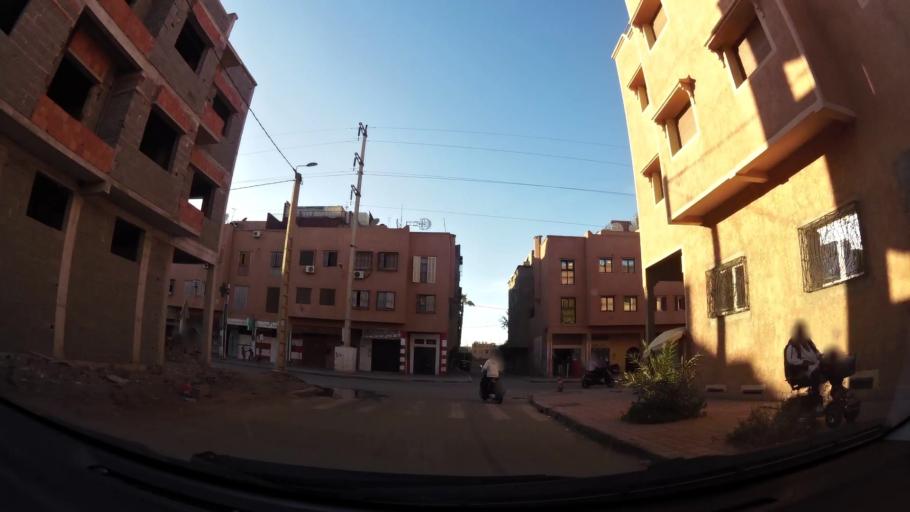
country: MA
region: Marrakech-Tensift-Al Haouz
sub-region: Marrakech
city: Marrakesh
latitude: 31.6175
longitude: -8.0559
